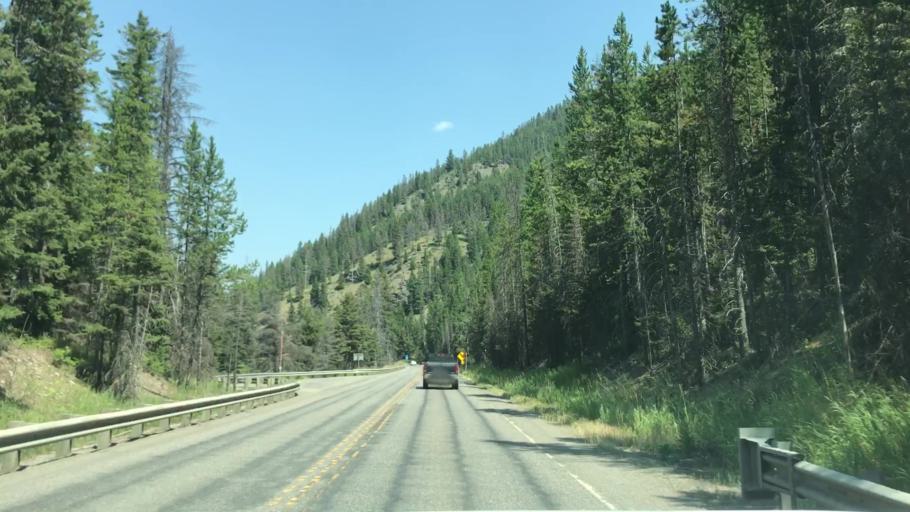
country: US
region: Montana
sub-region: Gallatin County
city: Big Sky
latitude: 45.3007
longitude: -111.1990
